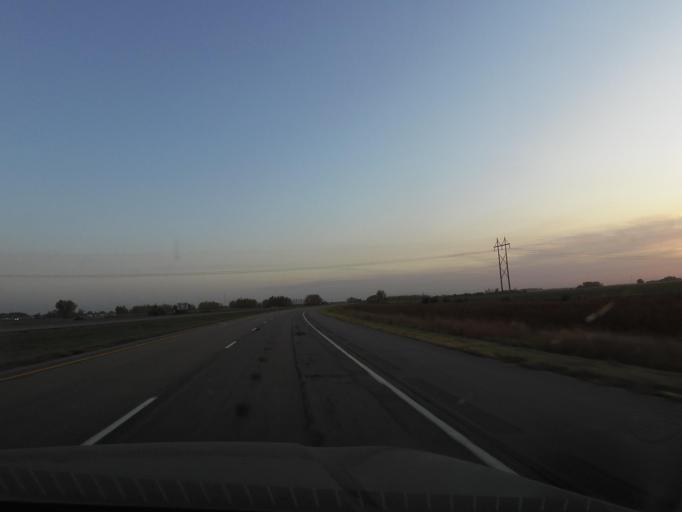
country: US
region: North Dakota
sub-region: Walsh County
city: Grafton
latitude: 48.5858
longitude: -97.1808
